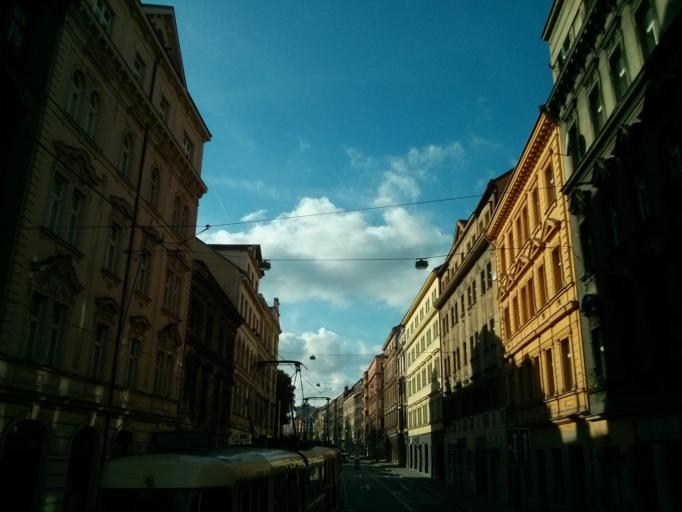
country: CZ
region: Praha
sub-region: Praha 1
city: Mala Strana
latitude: 50.0724
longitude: 14.3952
